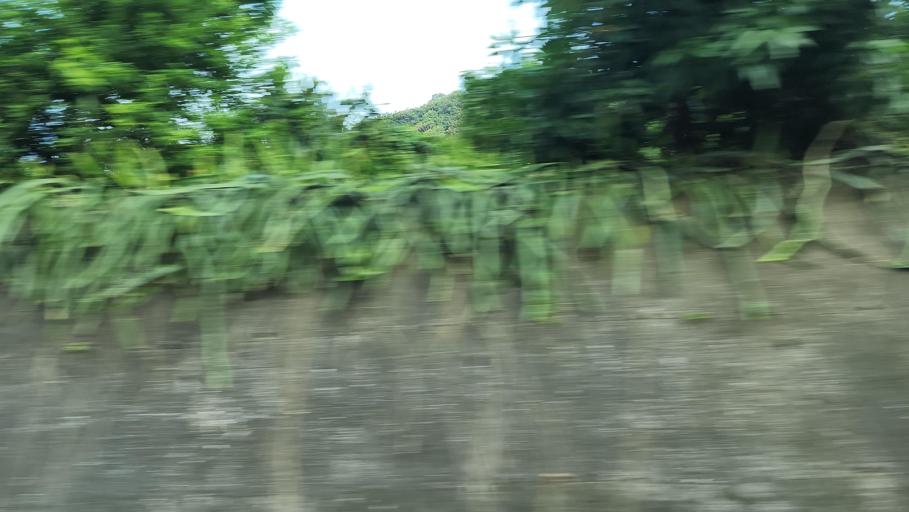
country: TW
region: Taiwan
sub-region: Keelung
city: Keelung
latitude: 25.1866
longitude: 121.6406
